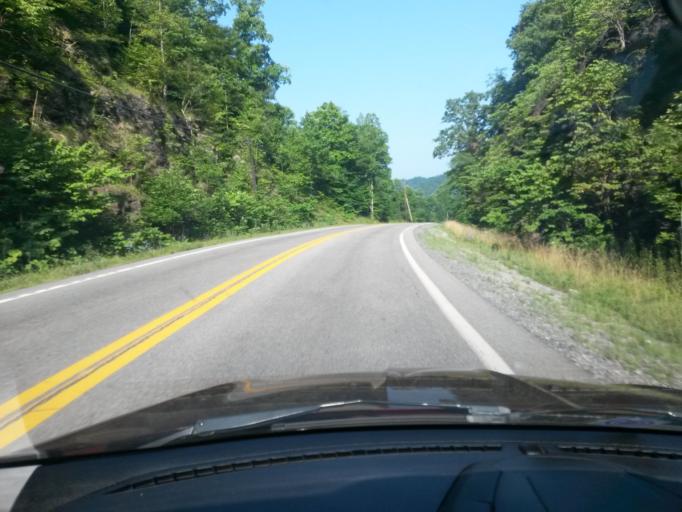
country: US
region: West Virginia
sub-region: Wyoming County
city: Pineville
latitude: 37.5517
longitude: -81.5520
